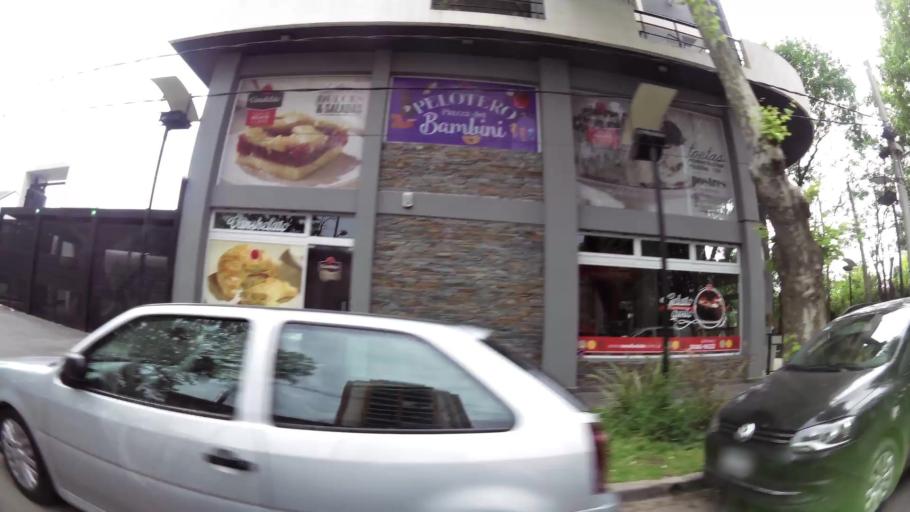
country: AR
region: Buenos Aires
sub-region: Partido de Quilmes
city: Quilmes
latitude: -34.8046
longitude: -58.2765
